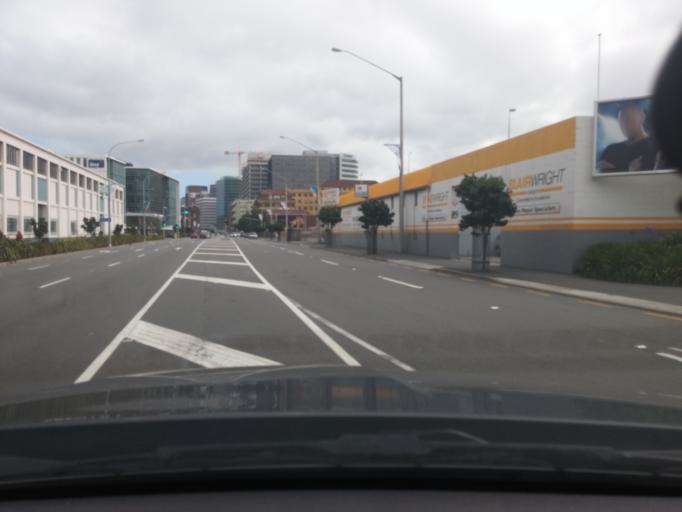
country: NZ
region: Wellington
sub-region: Wellington City
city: Wellington
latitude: -41.2774
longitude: 174.7832
